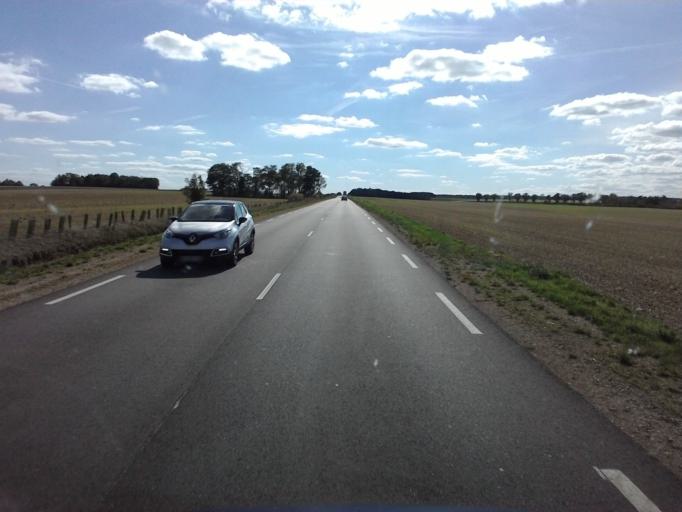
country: FR
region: Bourgogne
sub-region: Departement de la Cote-d'Or
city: Chatillon-sur-Seine
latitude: 47.8477
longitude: 4.5554
